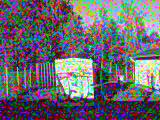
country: SE
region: Soedermanland
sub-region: Flens Kommun
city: Flen
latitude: 59.0614
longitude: 16.5949
